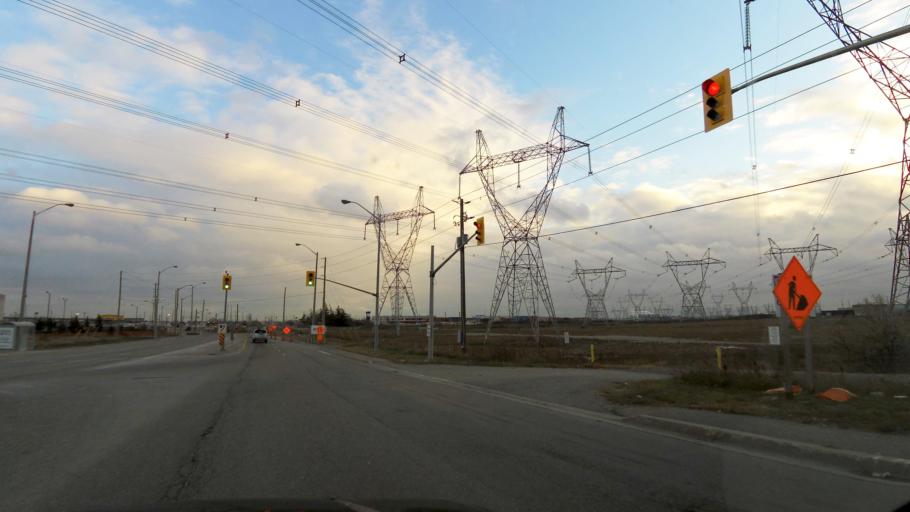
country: CA
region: Ontario
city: Brampton
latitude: 43.7103
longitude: -79.6743
